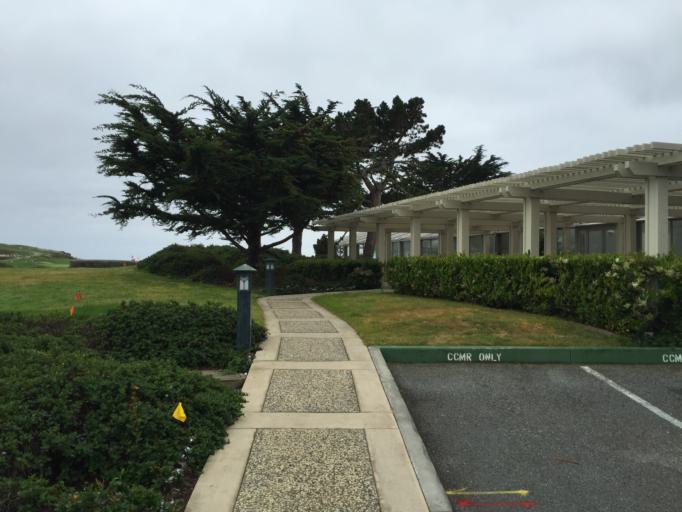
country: US
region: California
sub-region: San Mateo County
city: Half Moon Bay
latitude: 37.4361
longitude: -122.4410
